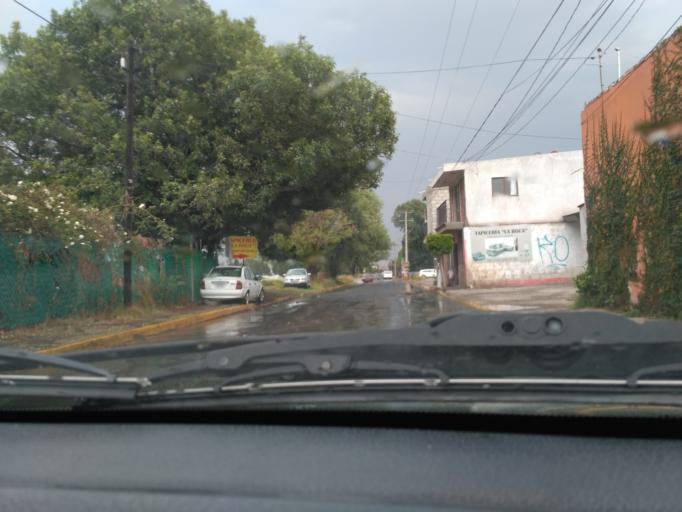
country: MX
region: Puebla
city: San Andres Cholula
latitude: 19.0549
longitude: -98.3056
